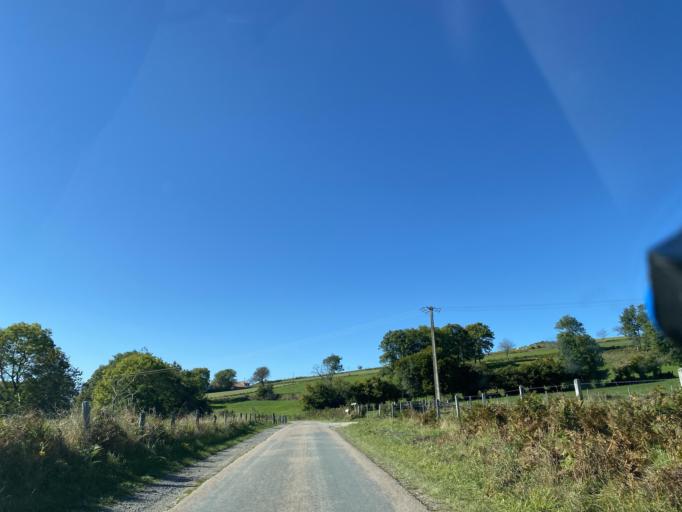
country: FR
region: Rhone-Alpes
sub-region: Departement de la Loire
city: Saint-Just-en-Chevalet
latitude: 45.9620
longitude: 3.8682
